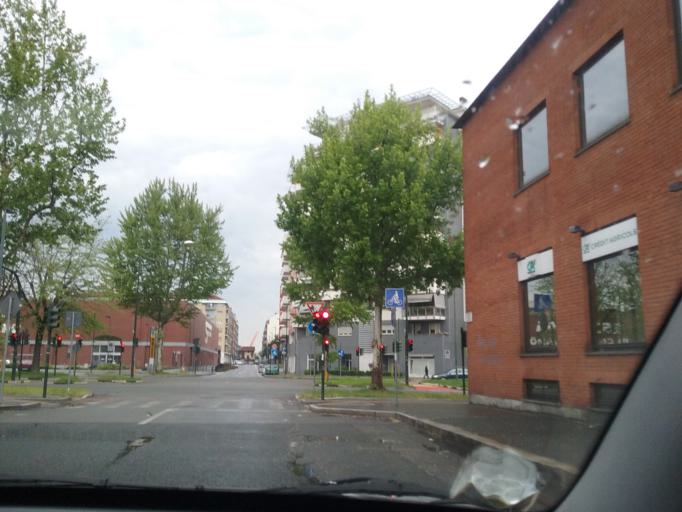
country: IT
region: Piedmont
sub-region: Provincia di Torino
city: Nichelino
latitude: 45.0207
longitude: 7.6526
